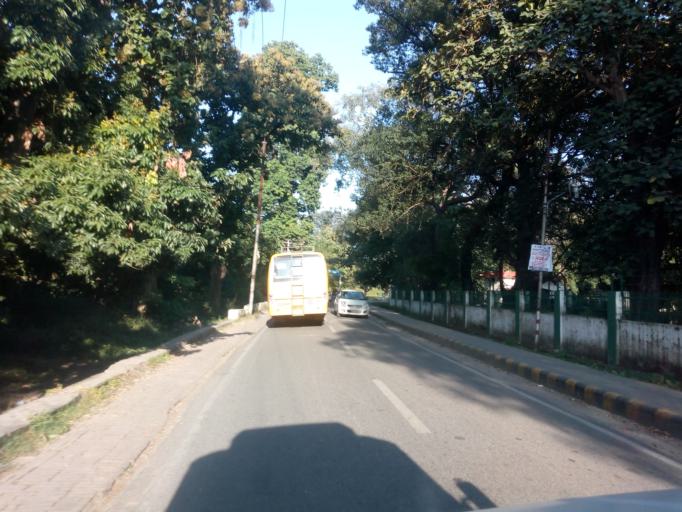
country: IN
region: Uttarakhand
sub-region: Dehradun
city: Dehradun
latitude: 30.3520
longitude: 78.0302
